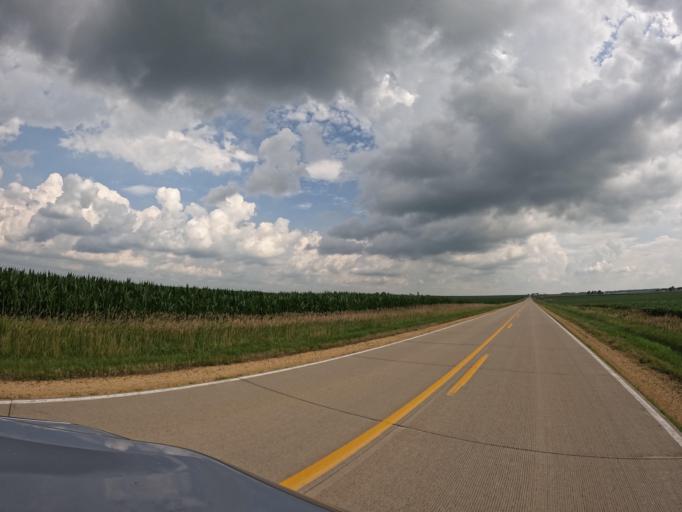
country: US
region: Iowa
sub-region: Clinton County
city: De Witt
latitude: 41.7930
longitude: -90.4132
